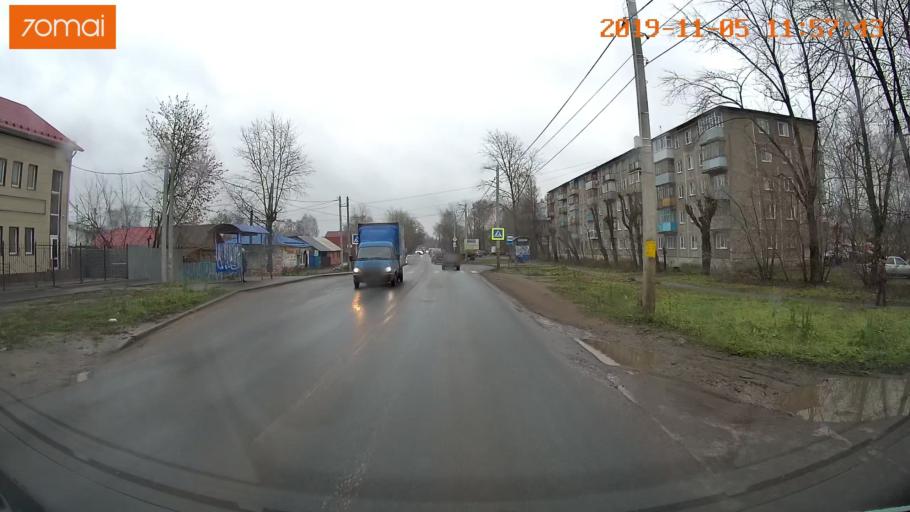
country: RU
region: Ivanovo
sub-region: Gorod Ivanovo
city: Ivanovo
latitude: 56.9825
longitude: 41.0360
